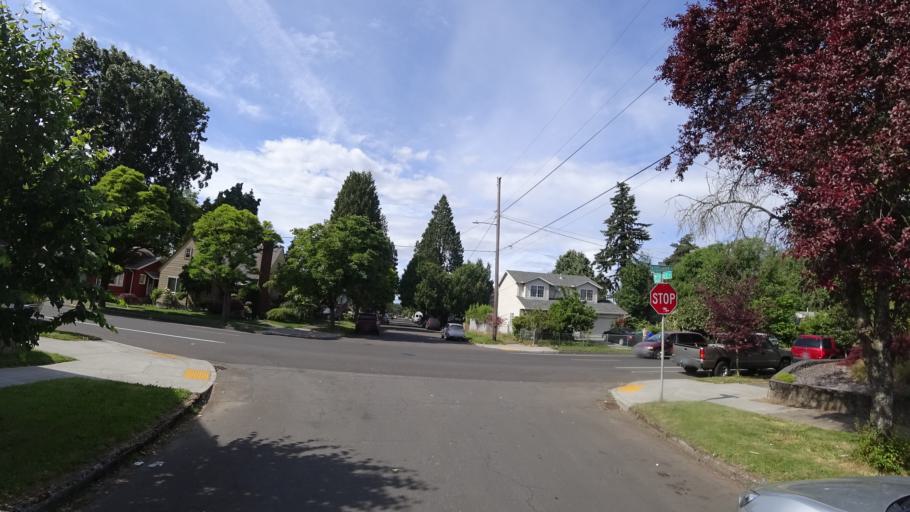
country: US
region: Washington
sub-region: Clark County
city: Vancouver
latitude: 45.5911
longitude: -122.7221
